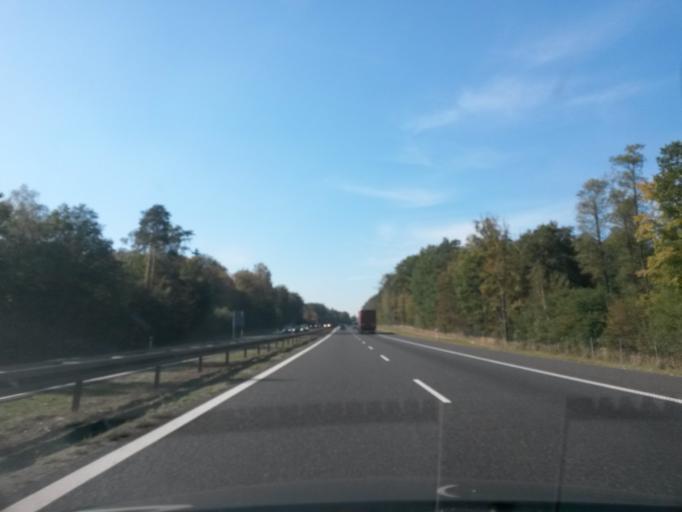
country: PL
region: Opole Voivodeship
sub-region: Powiat strzelecki
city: Ujazd
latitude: 50.4288
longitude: 18.3800
